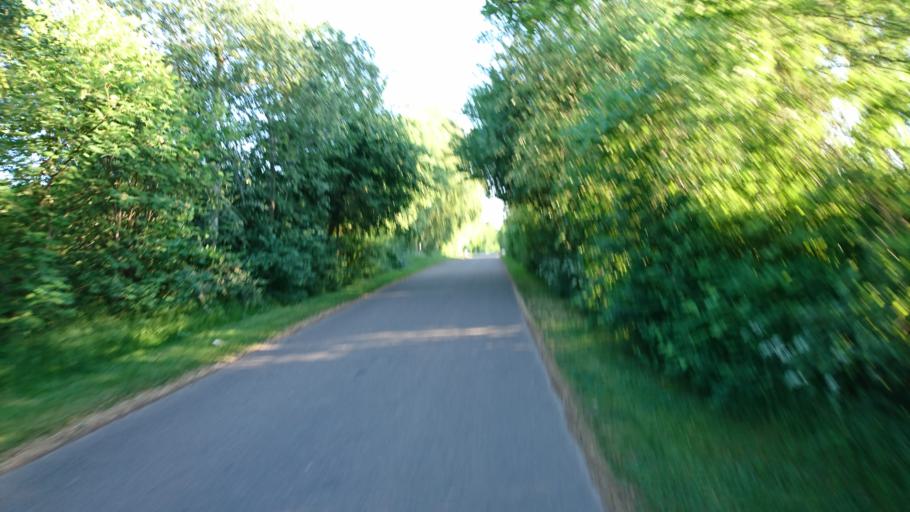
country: DK
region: Capital Region
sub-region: Ballerup Kommune
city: Ballerup
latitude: 55.7182
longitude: 12.3326
